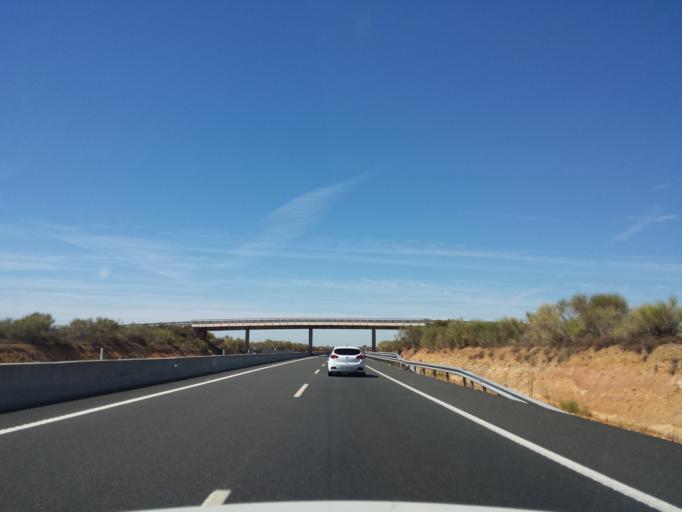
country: ES
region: Extremadura
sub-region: Provincia de Caceres
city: Casas de Miravete
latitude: 39.6738
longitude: -5.7437
